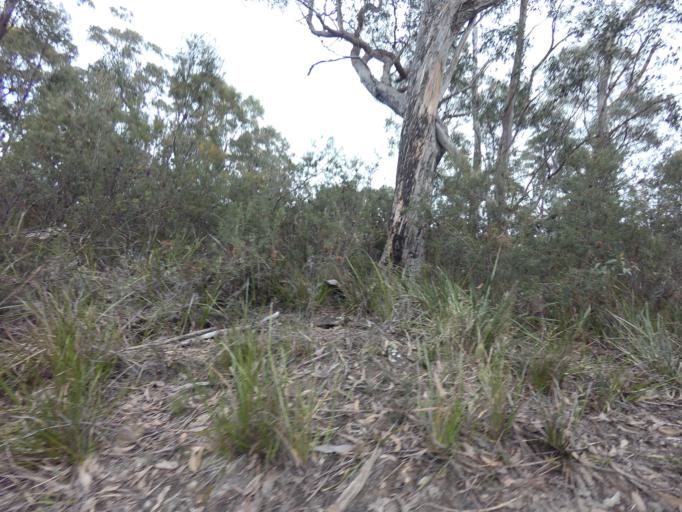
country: AU
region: Tasmania
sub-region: Huon Valley
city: Geeveston
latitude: -43.4725
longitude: 146.9316
